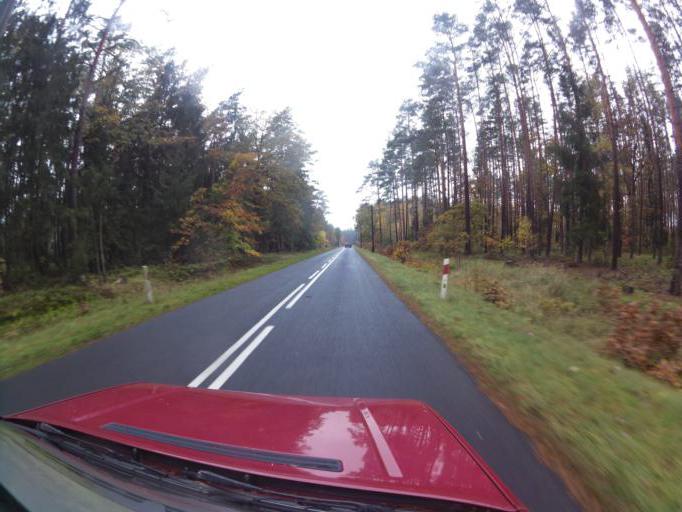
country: PL
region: West Pomeranian Voivodeship
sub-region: Powiat policki
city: Dobra
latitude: 53.5947
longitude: 14.3555
